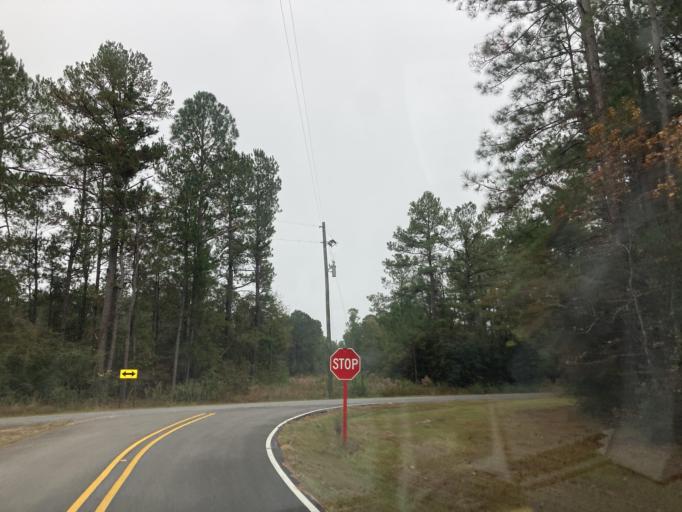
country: US
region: Mississippi
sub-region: Lamar County
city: Purvis
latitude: 31.0610
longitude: -89.3929
